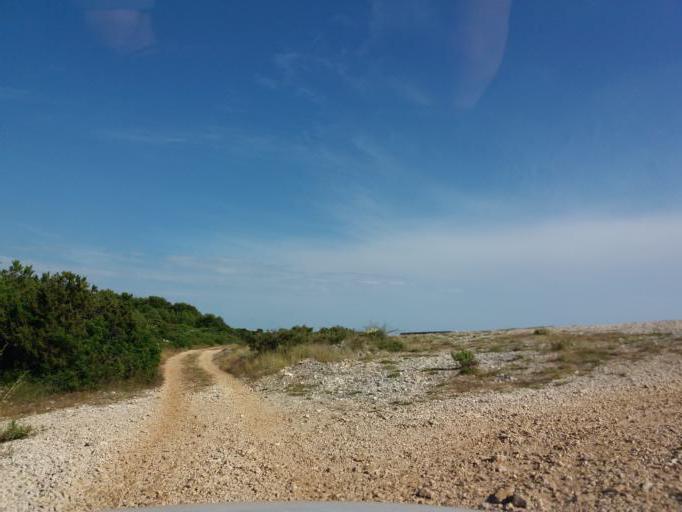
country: HR
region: Zadarska
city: Ugljan
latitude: 44.1299
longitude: 14.8646
